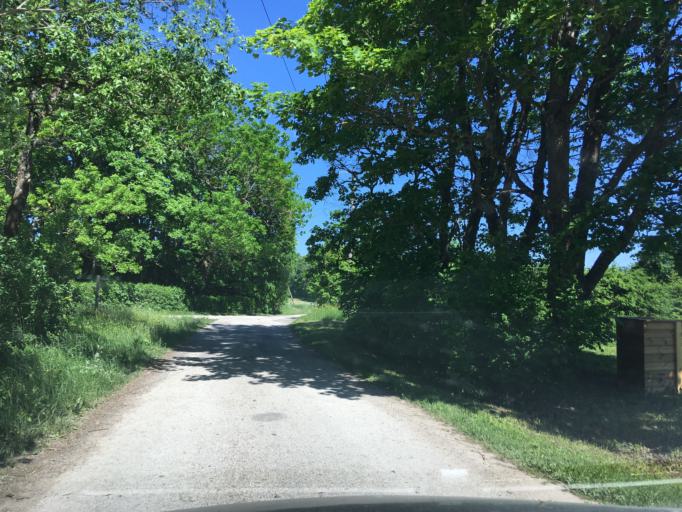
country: EE
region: Harju
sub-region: Rae vald
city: Vaida
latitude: 59.1575
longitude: 25.1263
